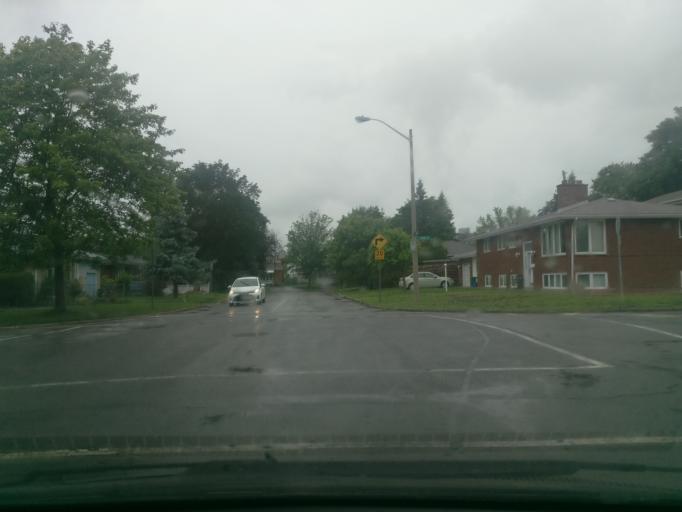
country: CA
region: Ontario
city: Ottawa
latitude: 45.4307
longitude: -75.6454
